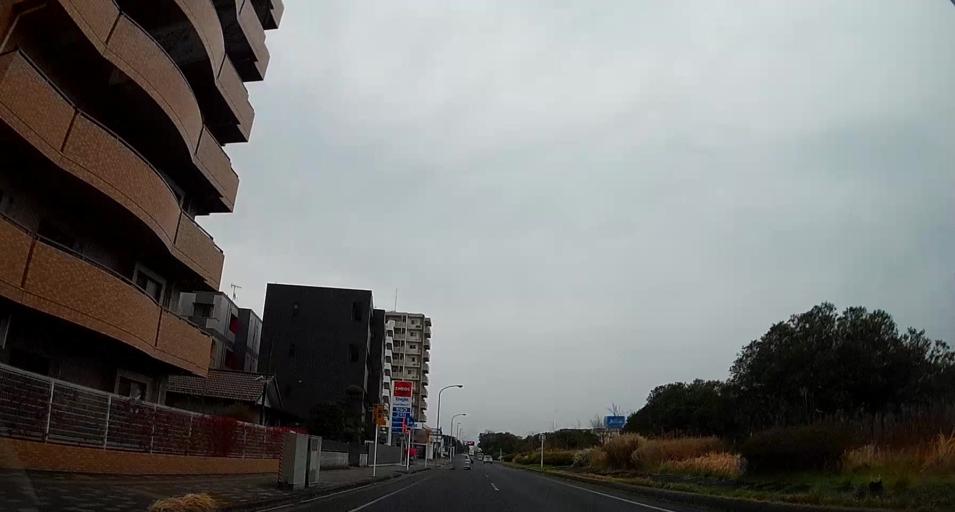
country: JP
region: Chiba
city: Chiba
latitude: 35.6533
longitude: 140.0577
